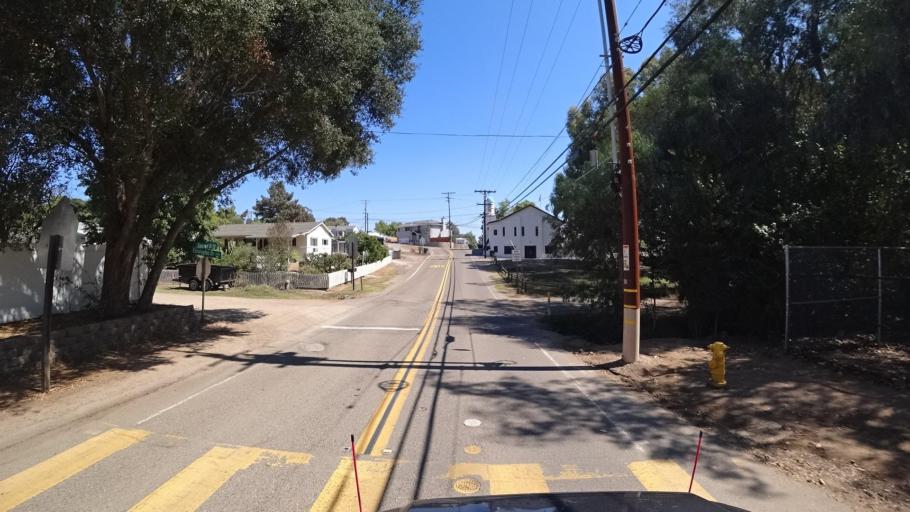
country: US
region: California
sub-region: San Diego County
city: Crest
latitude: 32.8059
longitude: -116.8655
